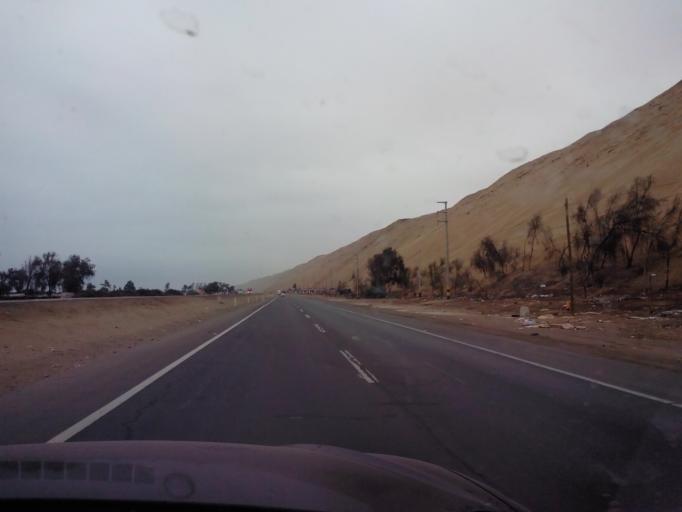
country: PE
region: Ica
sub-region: Provincia de Chincha
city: San Pedro
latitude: -13.3726
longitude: -76.2097
